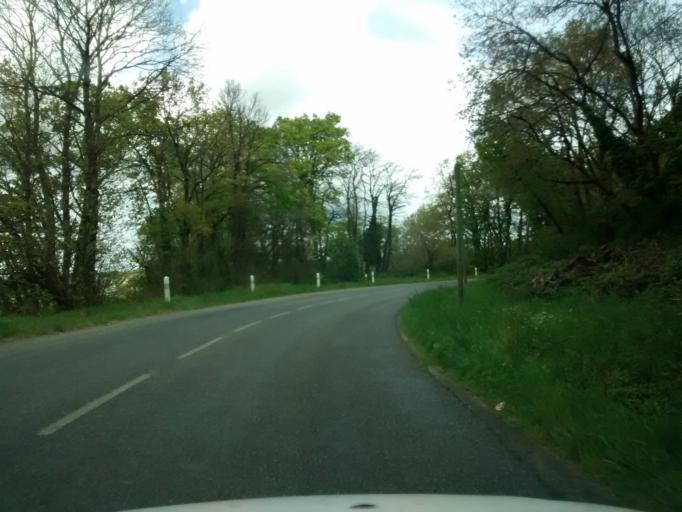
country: FR
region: Brittany
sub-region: Departement du Morbihan
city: Malestroit
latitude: 47.8055
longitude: -2.3703
